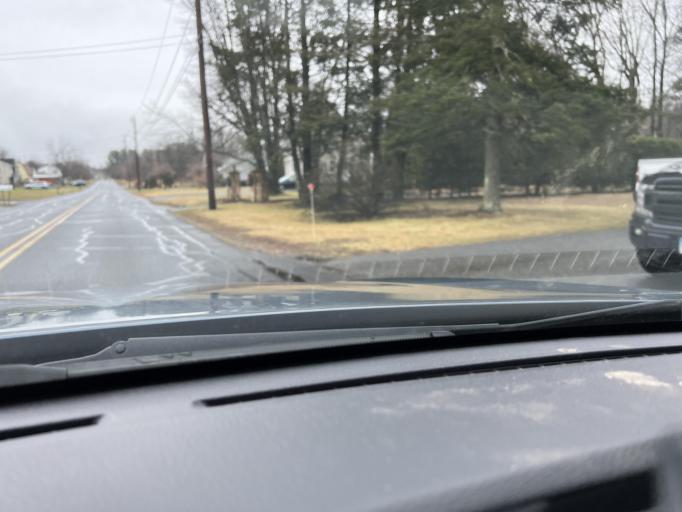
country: US
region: Massachusetts
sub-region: Hampden County
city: Southwick
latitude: 42.0415
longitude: -72.6979
